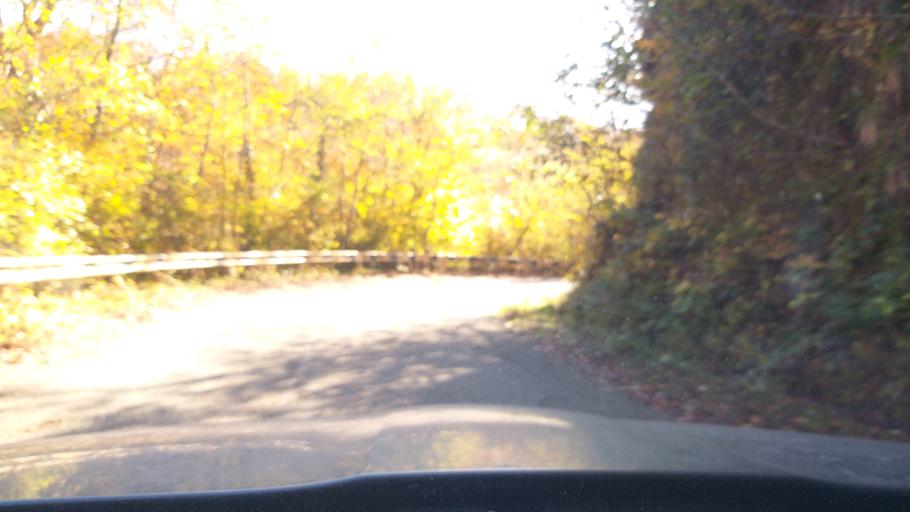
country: GE
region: Abkhazia
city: Bich'vinta
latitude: 43.1931
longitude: 40.4556
